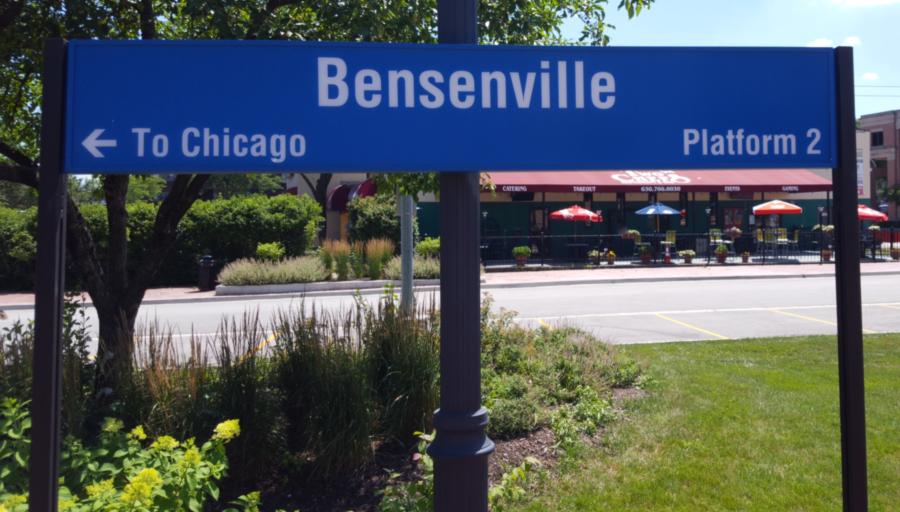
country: US
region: Illinois
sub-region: DuPage County
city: Bensenville
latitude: 41.9568
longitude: -87.9405
